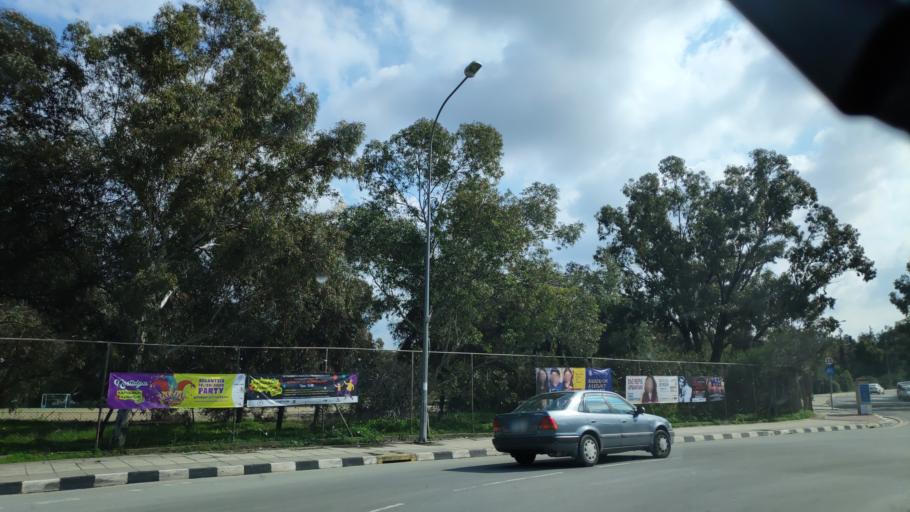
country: CY
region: Lefkosia
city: Nicosia
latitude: 35.1549
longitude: 33.3498
